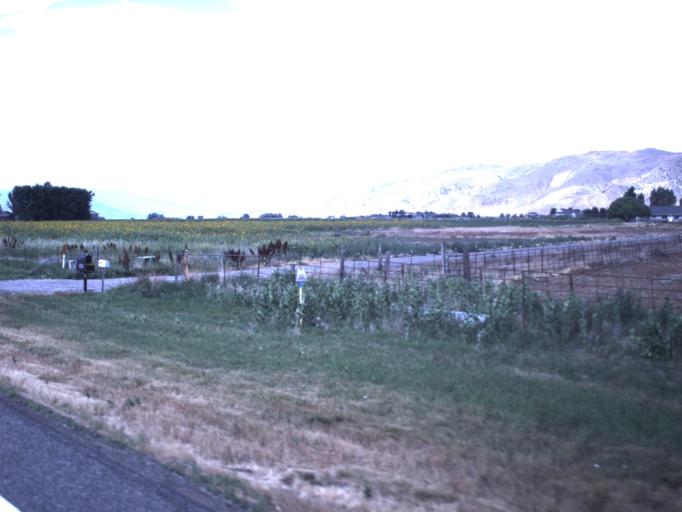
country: US
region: Utah
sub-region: Sevier County
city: Richfield
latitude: 38.7120
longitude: -112.1060
